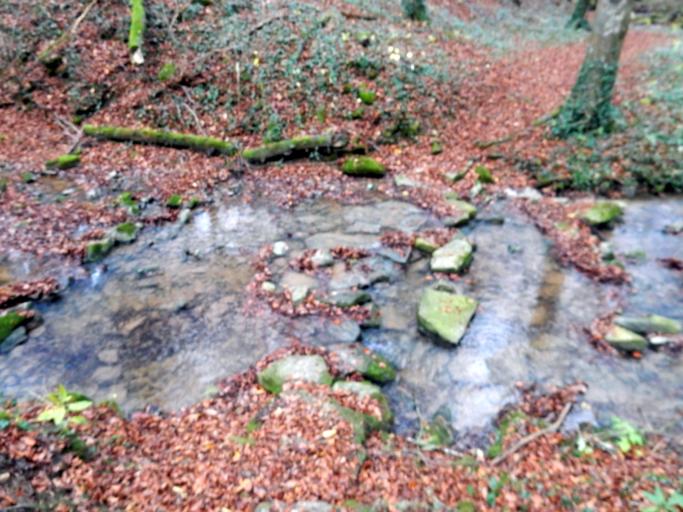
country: LU
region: Grevenmacher
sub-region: Canton d'Echternach
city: Rosport
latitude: 49.7697
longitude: 6.4886
